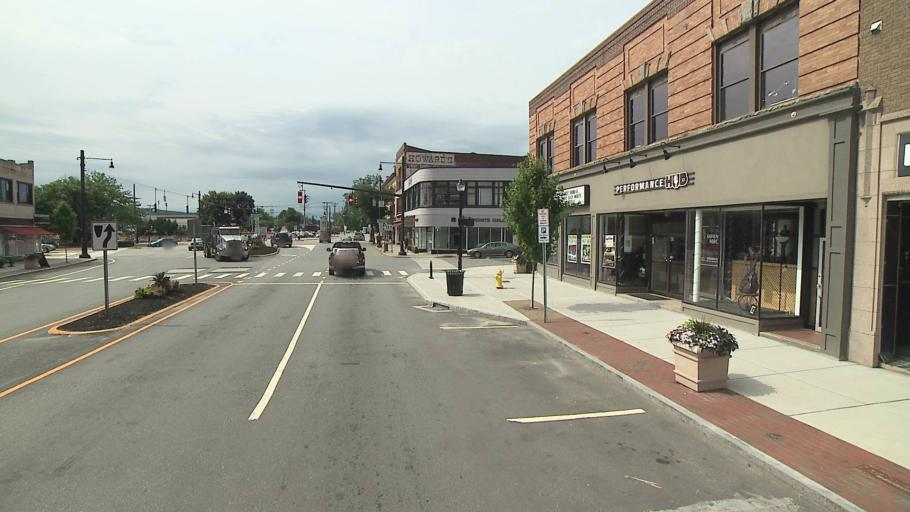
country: US
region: Connecticut
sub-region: Litchfield County
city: Torrington
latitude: 41.8015
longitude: -73.1215
